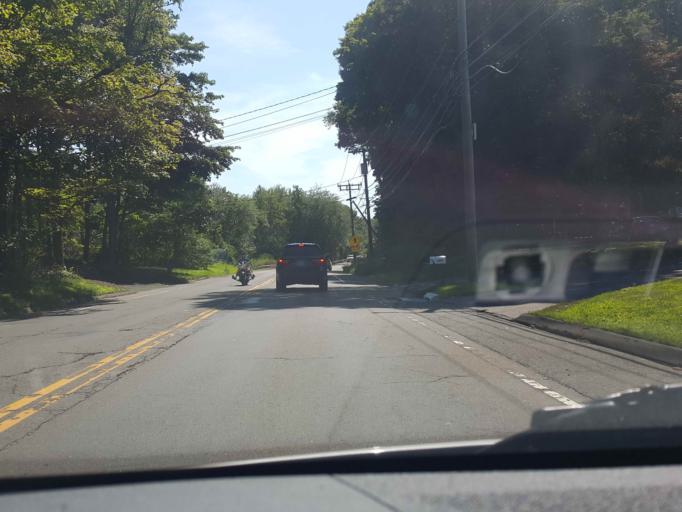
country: US
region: Connecticut
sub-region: New Haven County
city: North Branford
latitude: 41.3038
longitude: -72.7566
